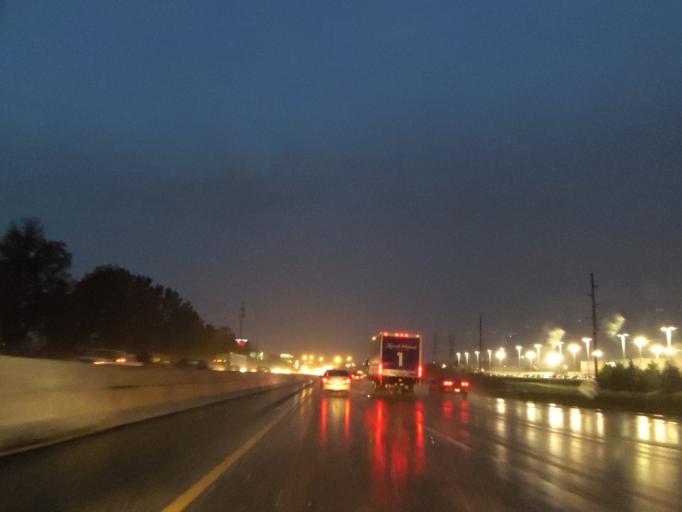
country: US
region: Tennessee
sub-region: Knox County
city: Farragut
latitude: 35.9029
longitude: -84.1579
